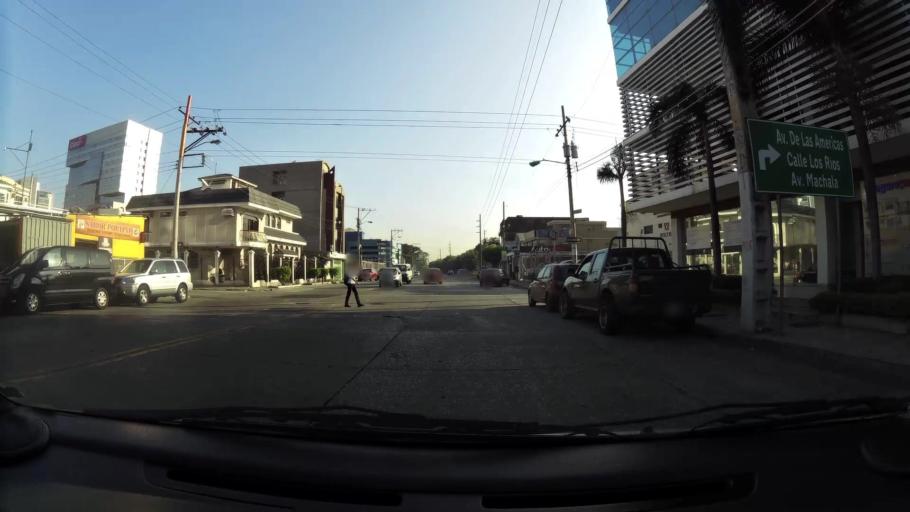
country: EC
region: Guayas
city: Eloy Alfaro
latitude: -2.1660
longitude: -79.8945
